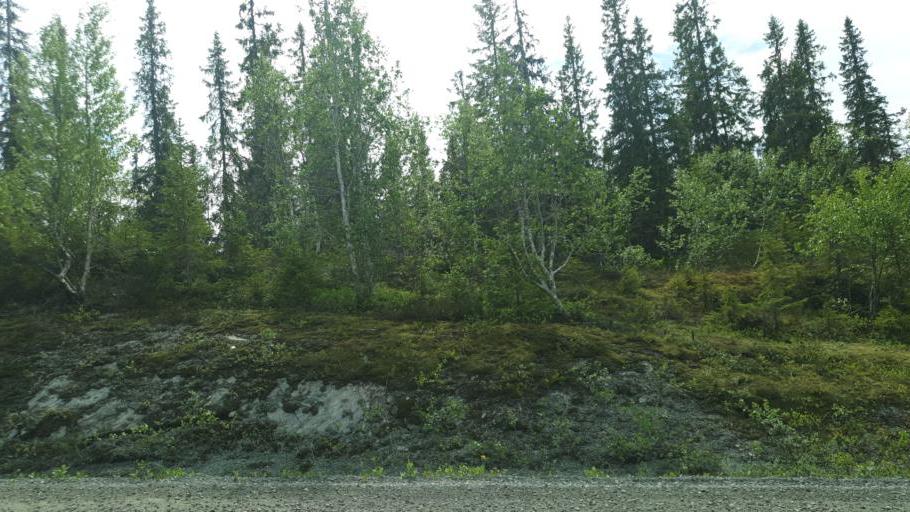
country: NO
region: Nord-Trondelag
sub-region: Leksvik
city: Leksvik
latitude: 63.6972
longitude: 10.4931
